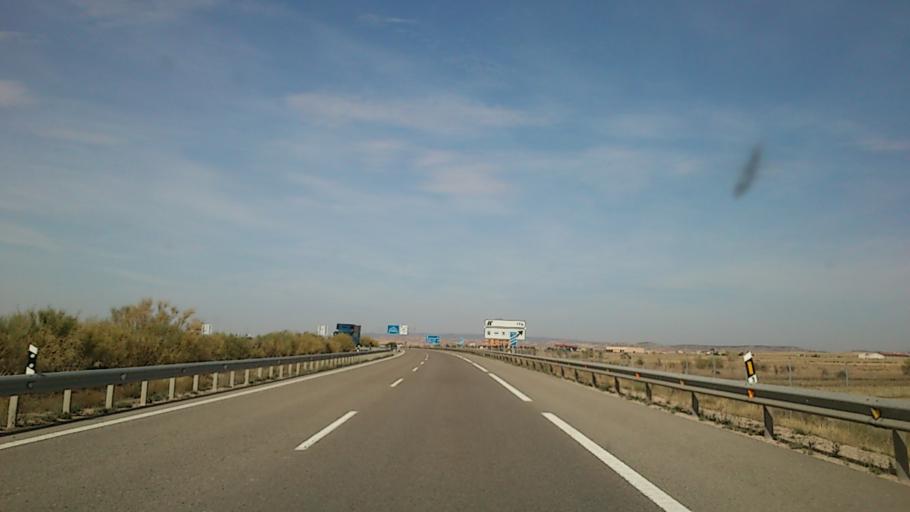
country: ES
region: Aragon
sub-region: Provincia de Teruel
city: Caminreal
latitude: 40.8308
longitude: -1.3160
